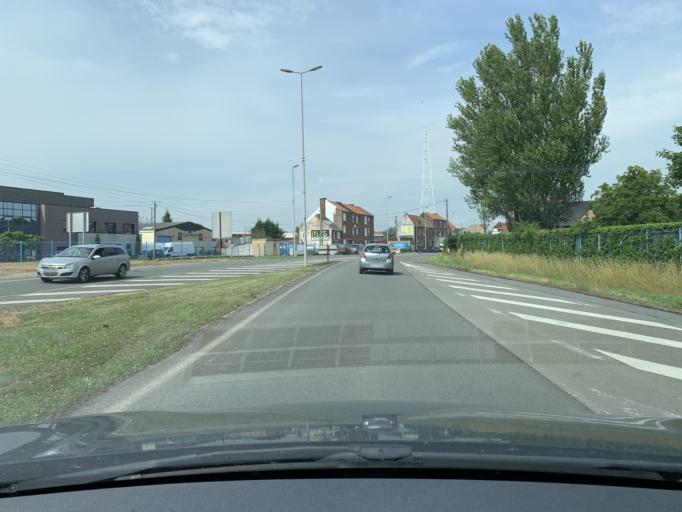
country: FR
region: Nord-Pas-de-Calais
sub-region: Departement du Nord
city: Douai
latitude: 50.3594
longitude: 3.0573
